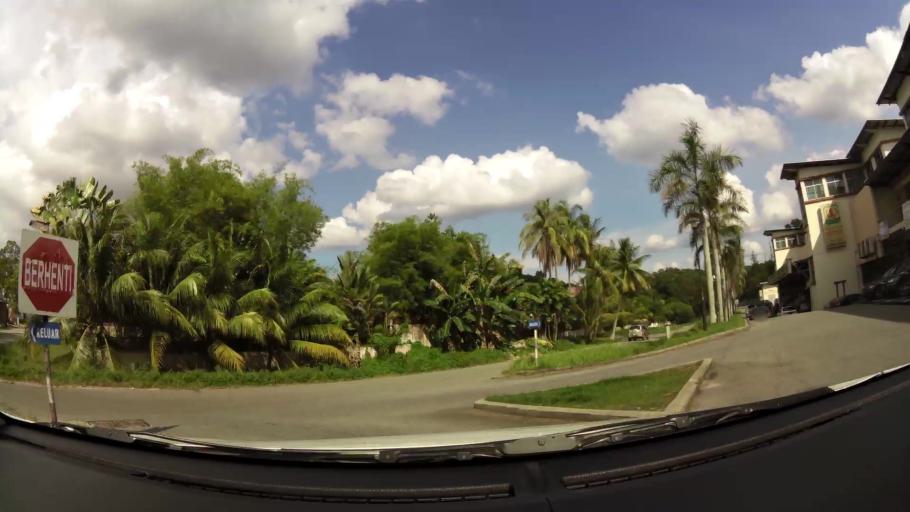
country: BN
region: Brunei and Muara
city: Bandar Seri Begawan
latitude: 4.9503
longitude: 114.9675
